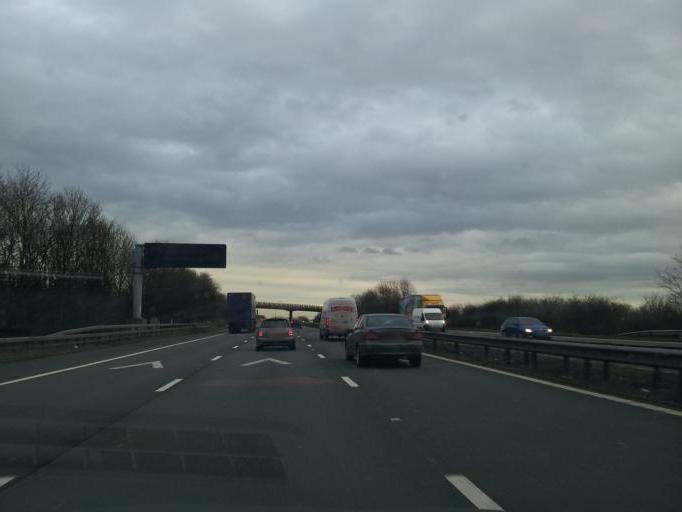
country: GB
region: England
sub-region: Warwickshire
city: Long Lawford
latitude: 52.4210
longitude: -1.3027
